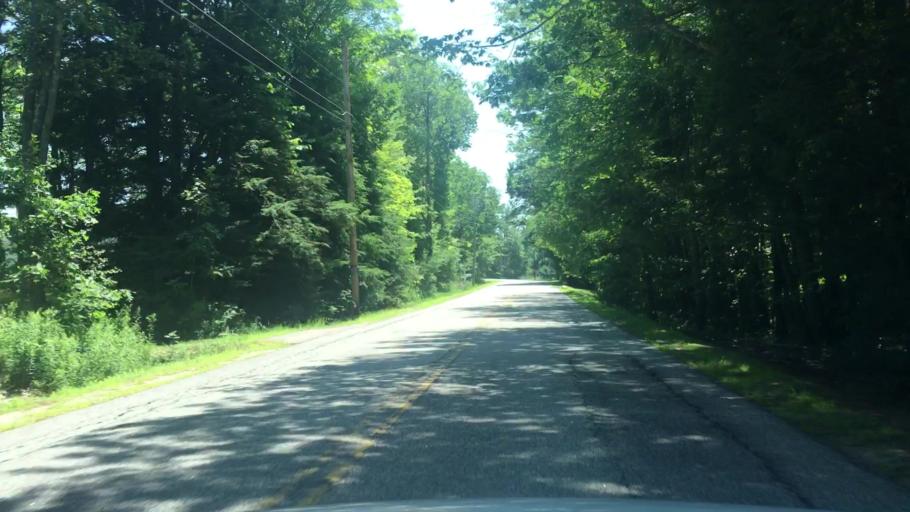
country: US
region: Maine
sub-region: Cumberland County
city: Falmouth
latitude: 43.7443
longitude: -70.2695
